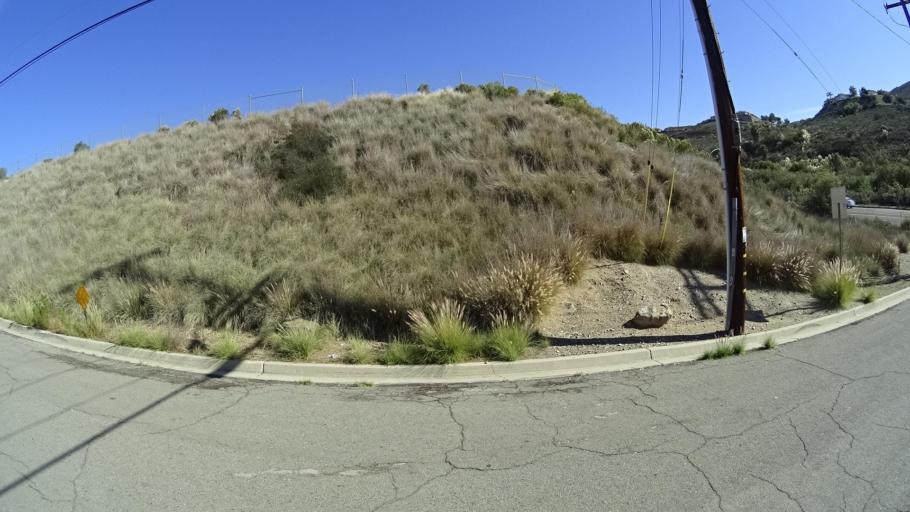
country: US
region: California
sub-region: San Diego County
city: La Presa
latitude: 32.7200
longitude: -116.9738
